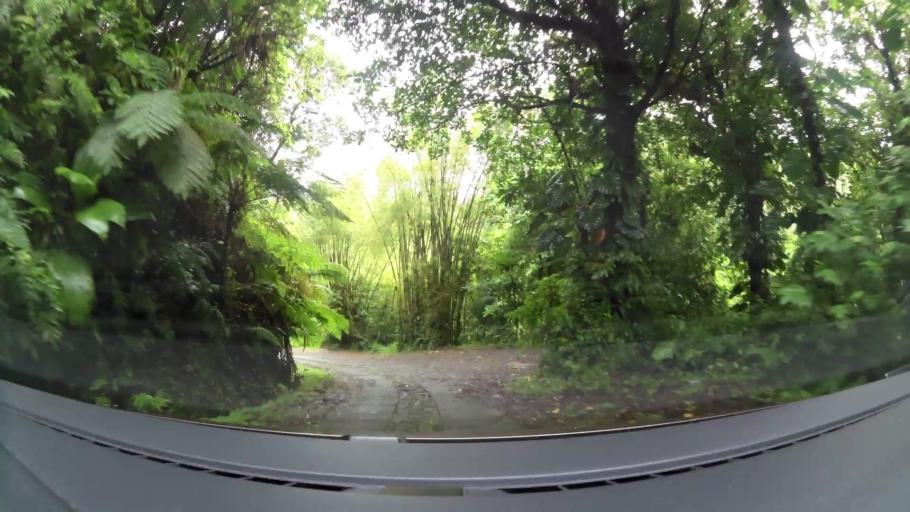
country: GP
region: Guadeloupe
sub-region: Guadeloupe
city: Trois-Rivieres
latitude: 16.0372
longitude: -61.6379
